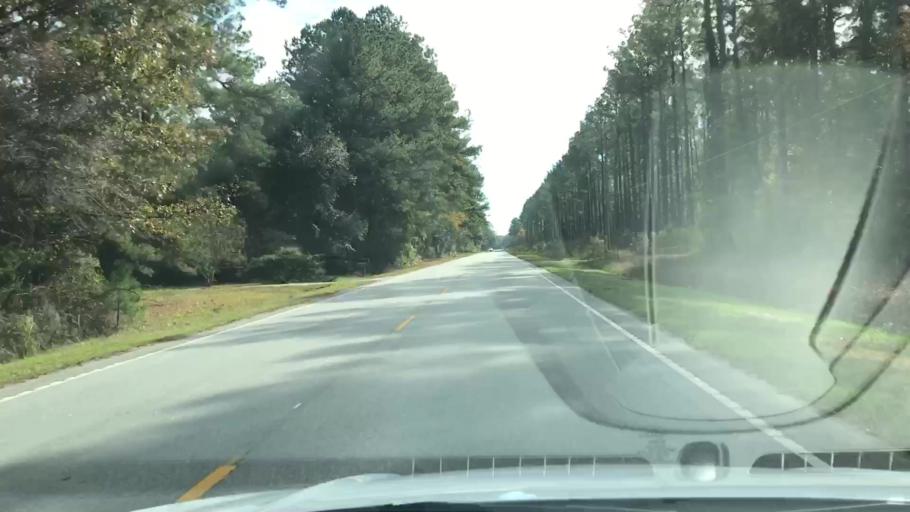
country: US
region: South Carolina
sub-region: Colleton County
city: Walterboro
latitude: 32.7886
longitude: -80.4781
